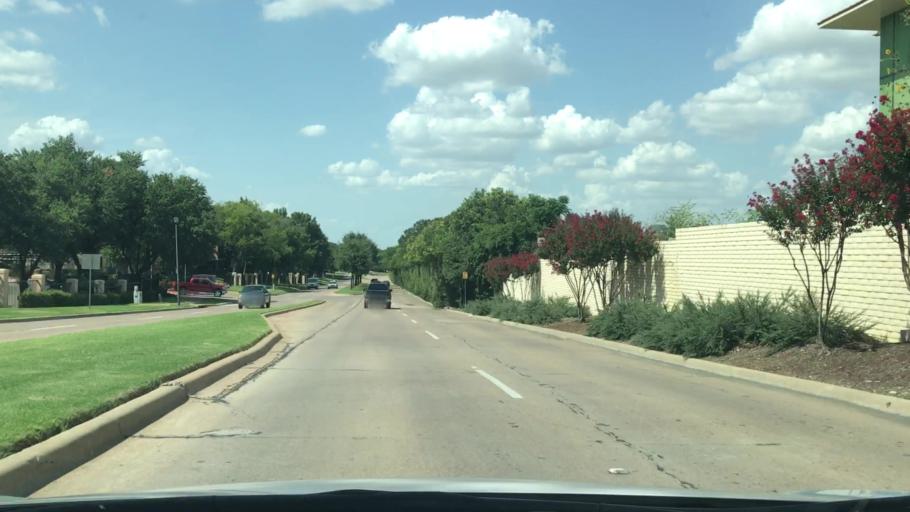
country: US
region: Texas
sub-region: Dallas County
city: Irving
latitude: 32.8554
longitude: -96.9504
